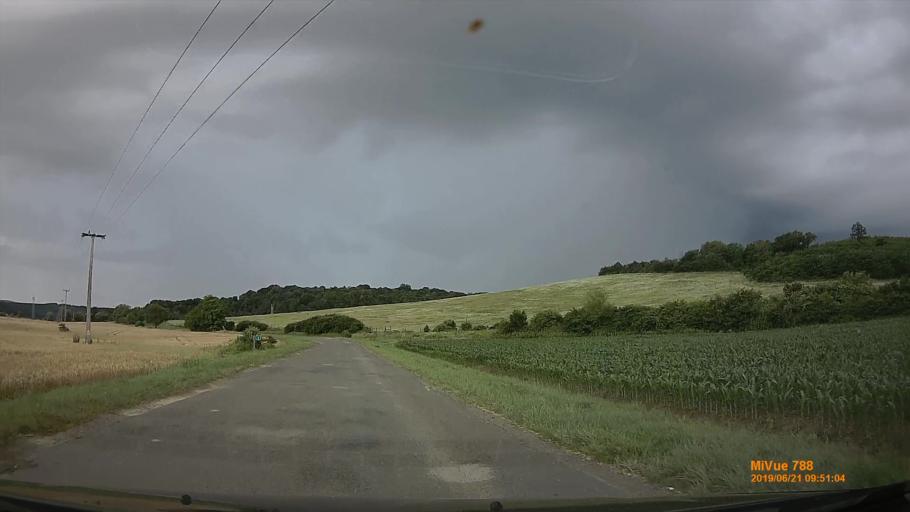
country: HU
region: Baranya
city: Sasd
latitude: 46.2554
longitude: 18.0250
